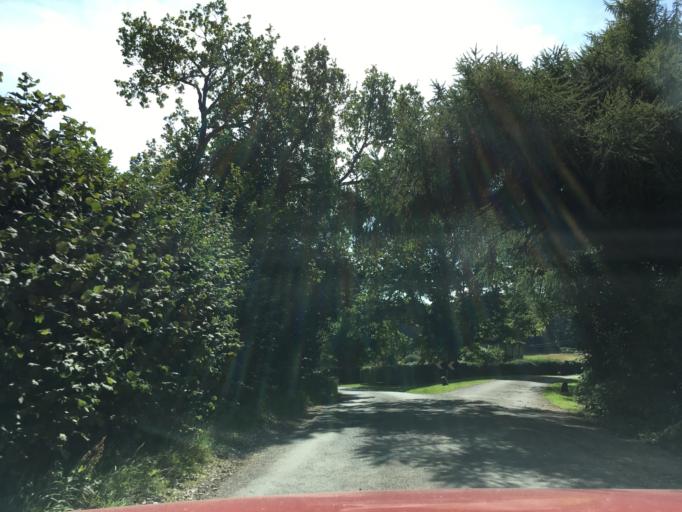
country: GB
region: England
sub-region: Hampshire
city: Highclere
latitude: 51.2899
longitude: -1.3710
